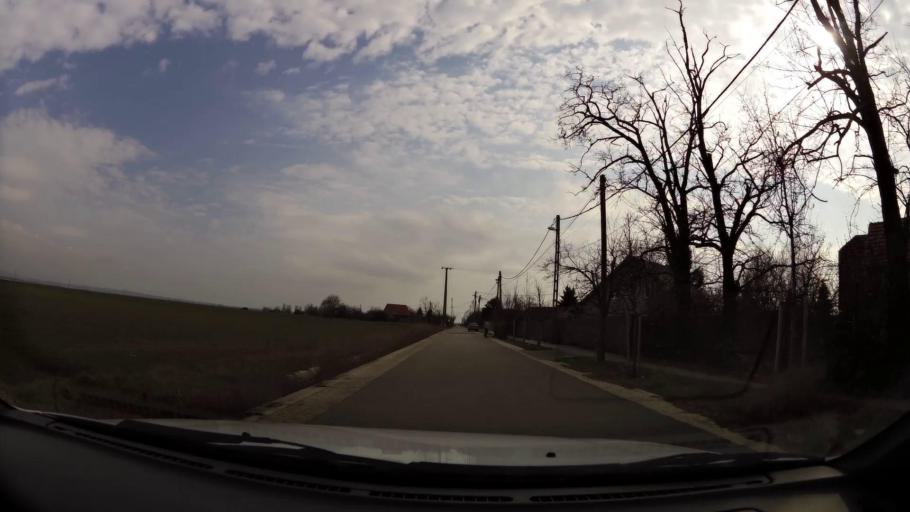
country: HU
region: Pest
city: Csomor
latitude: 47.5263
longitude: 19.2366
